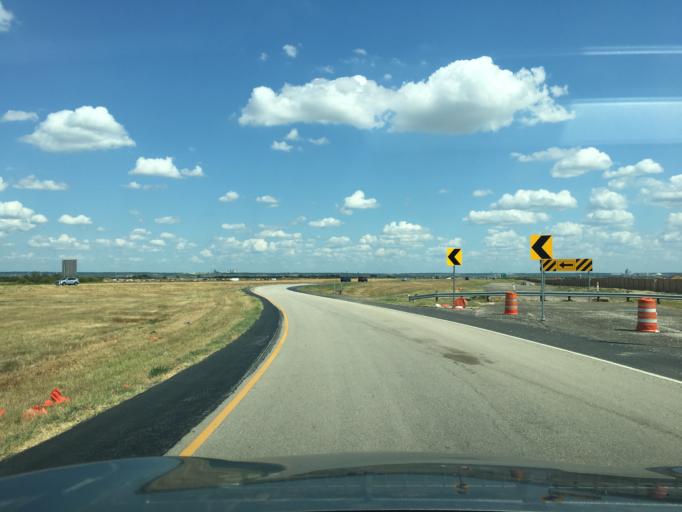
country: US
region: Texas
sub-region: Tarrant County
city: Mansfield
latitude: 32.5328
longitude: -97.1014
